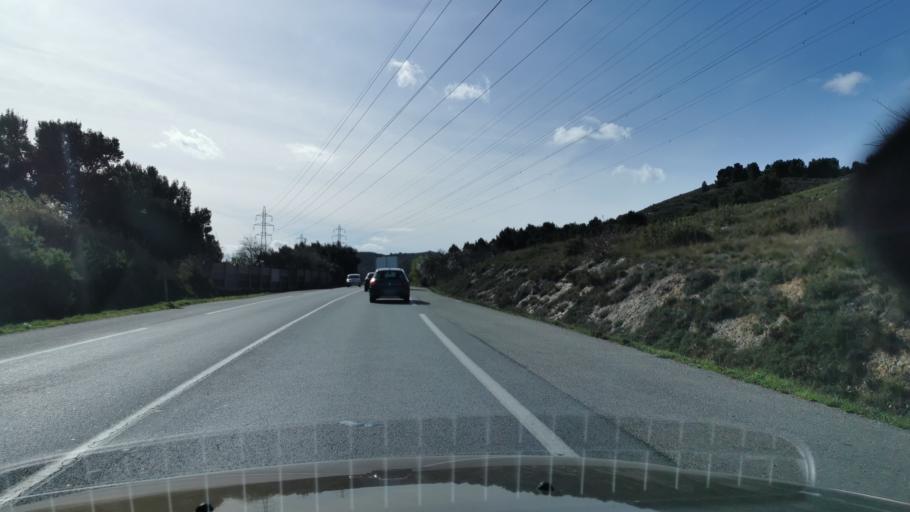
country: FR
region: Languedoc-Roussillon
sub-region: Departement de l'Aude
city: Narbonne
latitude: 43.1856
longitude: 2.9714
